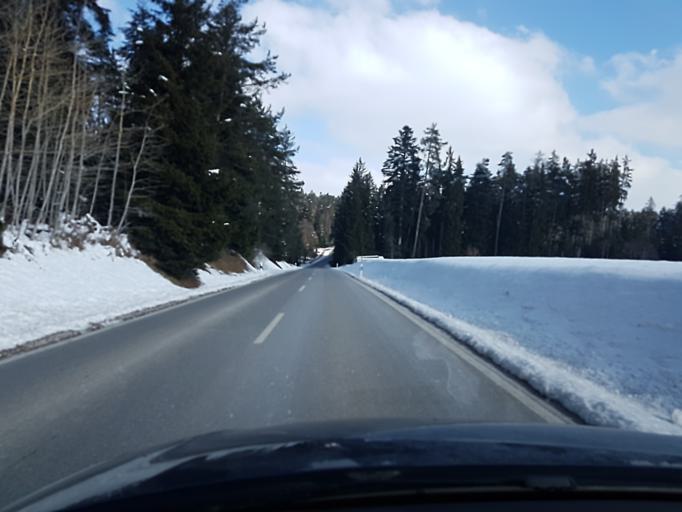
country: DE
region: Baden-Wuerttemberg
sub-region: Freiburg Region
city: Konigsfeld im Schwarzwald
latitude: 48.1580
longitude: 8.4535
